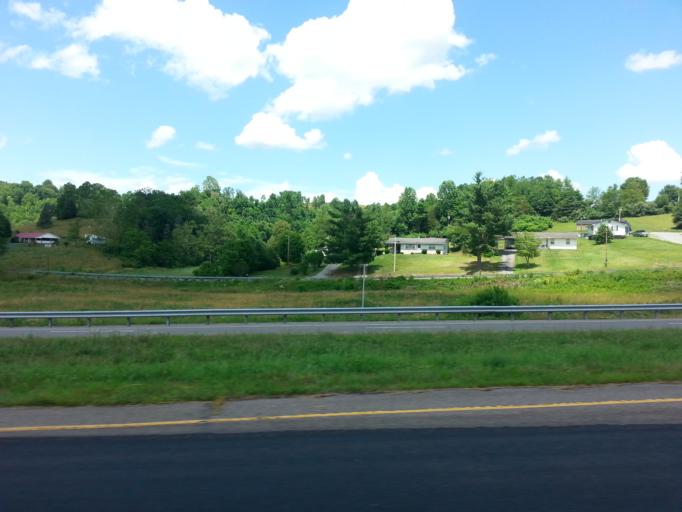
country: US
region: Virginia
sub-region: Lee County
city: Jonesville
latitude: 36.6710
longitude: -83.2032
